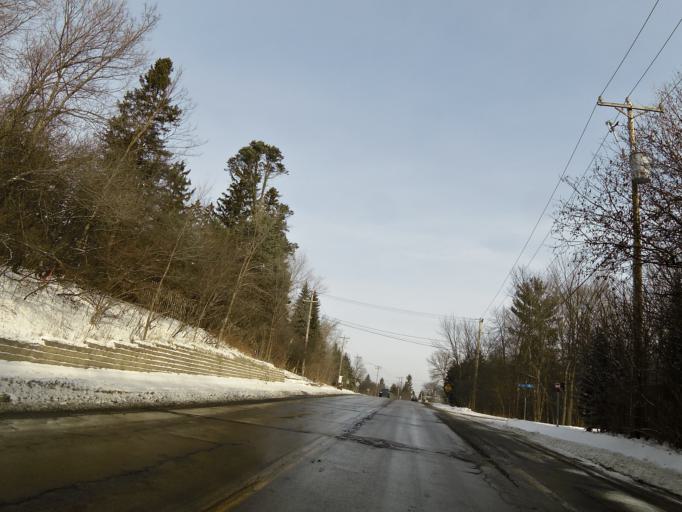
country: US
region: Minnesota
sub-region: Hennepin County
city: Minnetonka
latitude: 44.9065
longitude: -93.5054
